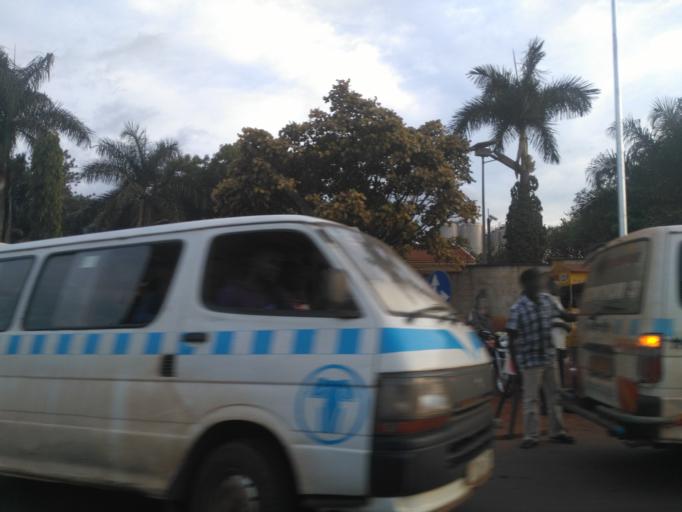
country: UG
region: Central Region
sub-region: Buikwe District
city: Njeru
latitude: 0.4399
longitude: 33.1787
